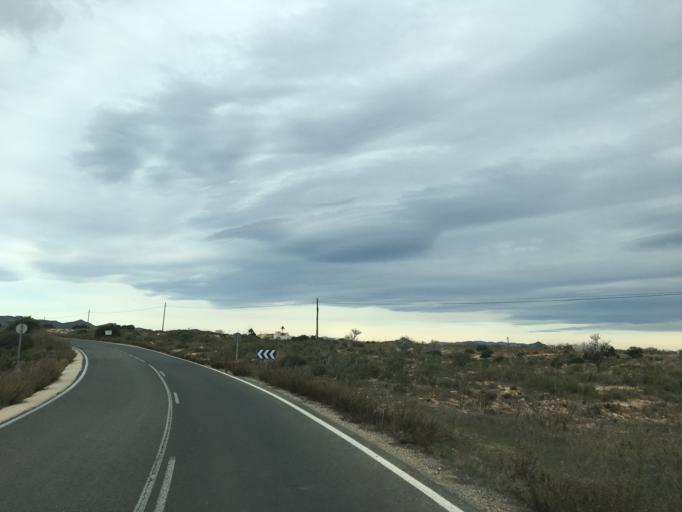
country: ES
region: Murcia
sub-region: Murcia
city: Fuente-Alamo de Murcia
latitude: 37.6191
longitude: -1.0729
